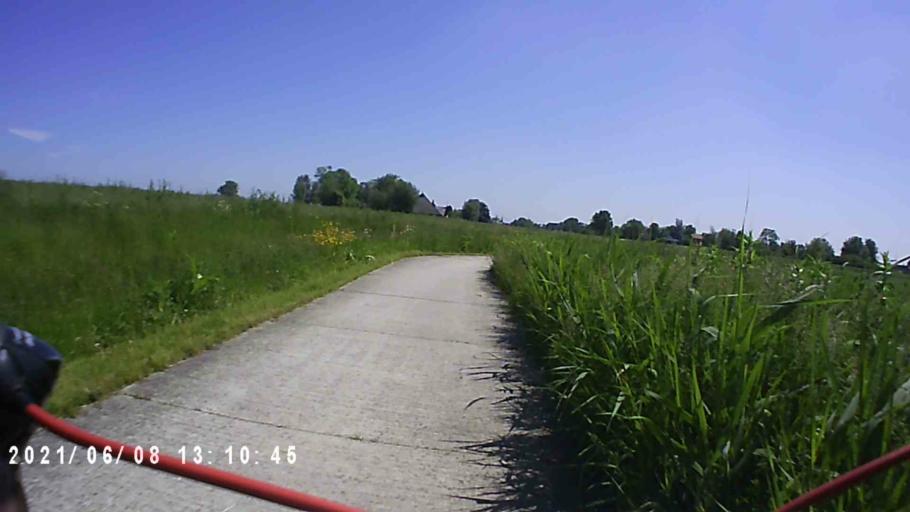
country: NL
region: Groningen
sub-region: Gemeente Zuidhorn
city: Zuidhorn
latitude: 53.2286
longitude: 6.4344
